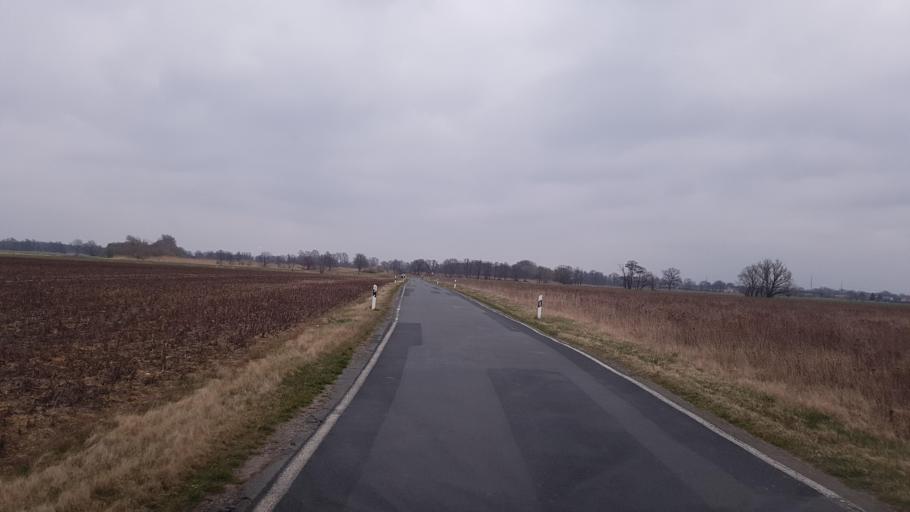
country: DE
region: Saxony
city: Nauwalde
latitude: 51.4250
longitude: 13.3686
